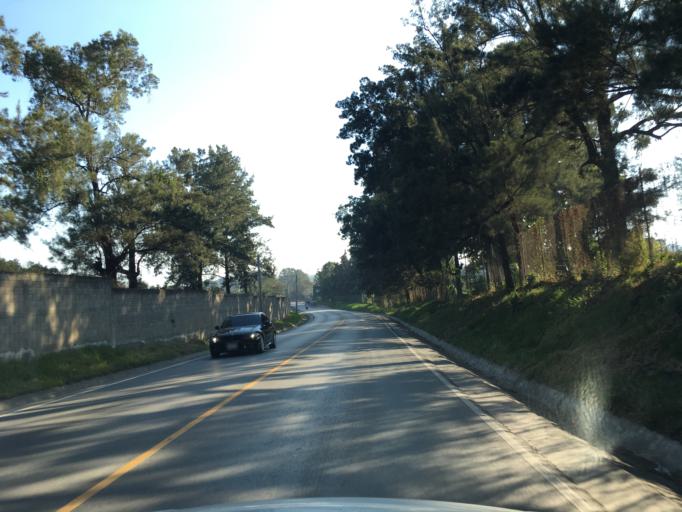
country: GT
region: Guatemala
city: Villa Nueva
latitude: 14.5296
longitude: -90.6168
